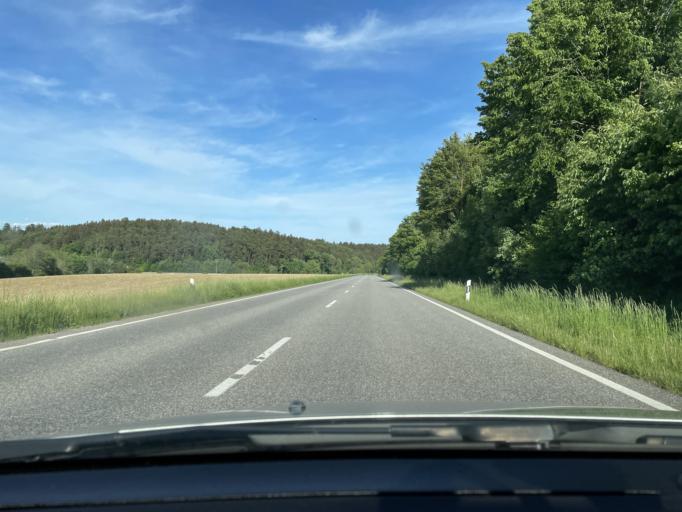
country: DE
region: Bavaria
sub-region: Lower Bavaria
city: Pfeffenhausen
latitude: 48.6534
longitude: 11.9608
